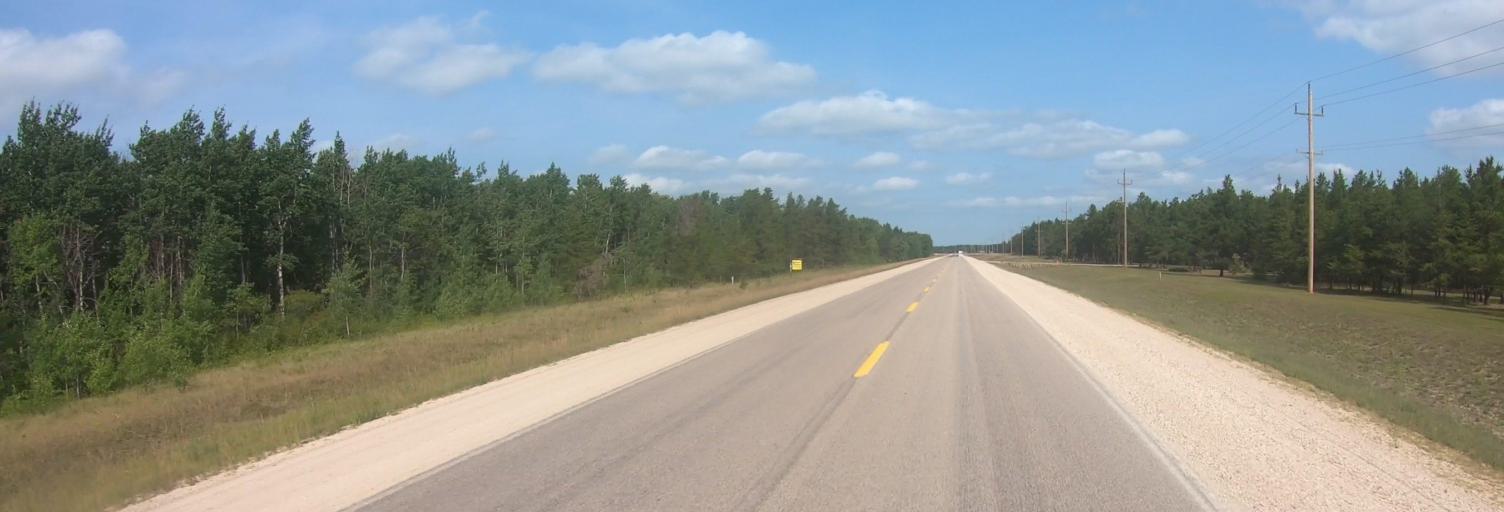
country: CA
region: Manitoba
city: La Broquerie
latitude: 49.2542
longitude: -96.3561
